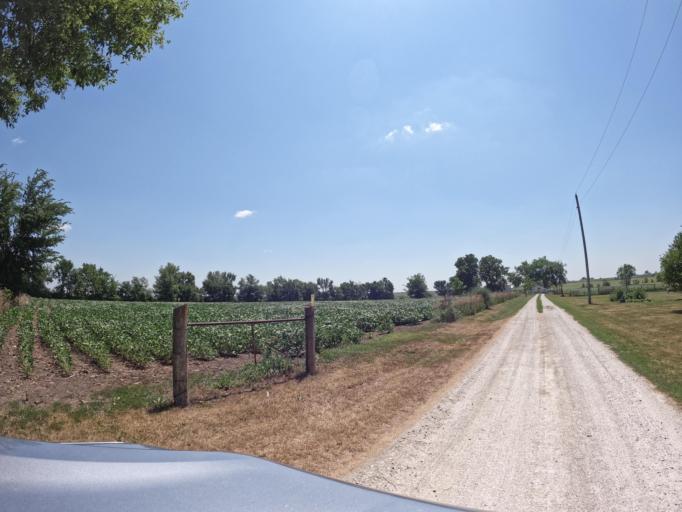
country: US
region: Iowa
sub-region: Keokuk County
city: Sigourney
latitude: 41.2743
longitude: -92.1654
